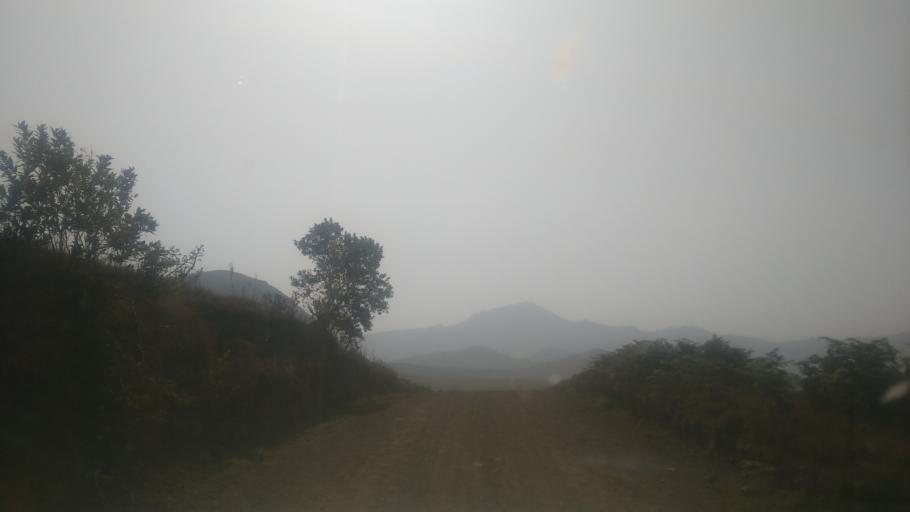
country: CM
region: Littoral
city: Nkongsamba
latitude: 5.0437
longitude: 9.8174
